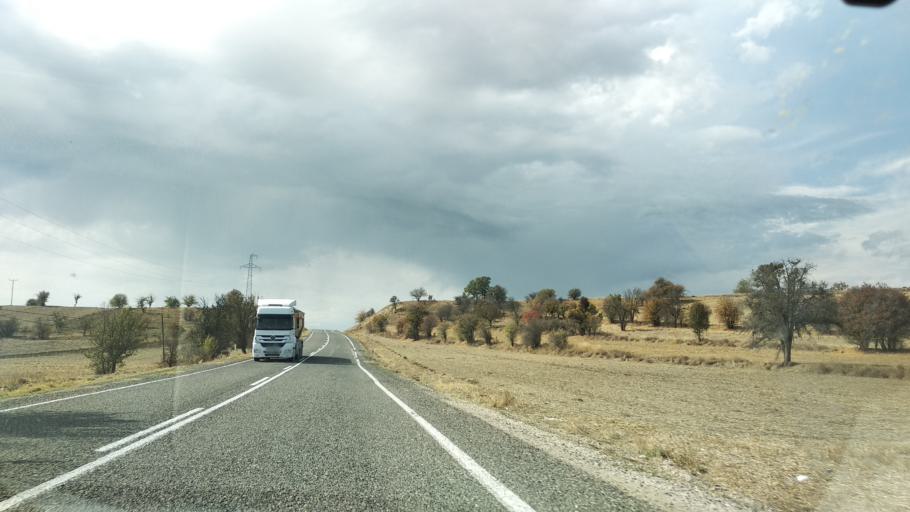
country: TR
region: Bolu
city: Seben
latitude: 40.3746
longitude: 31.5141
